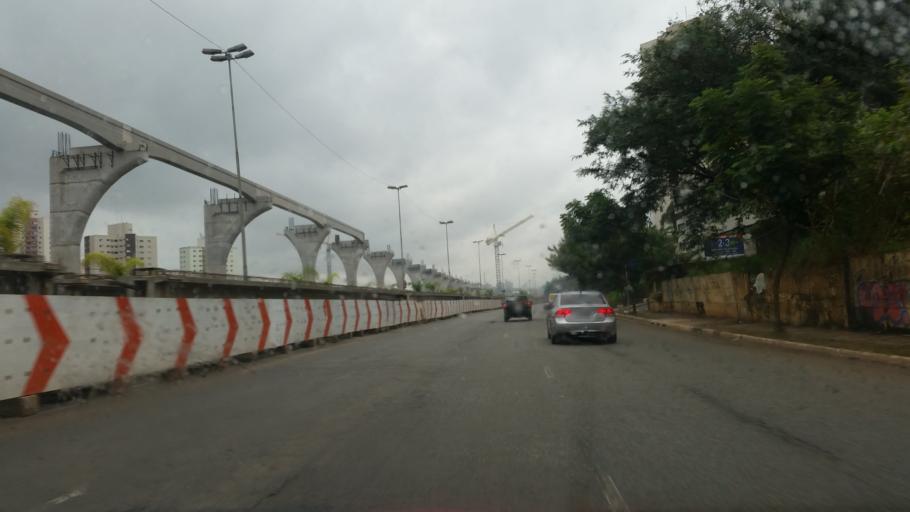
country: BR
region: Sao Paulo
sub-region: Diadema
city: Diadema
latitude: -23.6370
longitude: -46.6638
